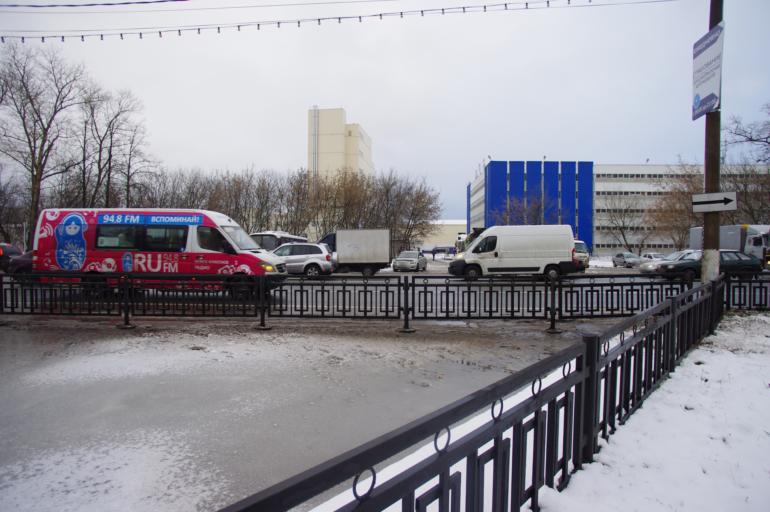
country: RU
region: Moskovskaya
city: Krasnogorsk
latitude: 55.8083
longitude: 37.3337
